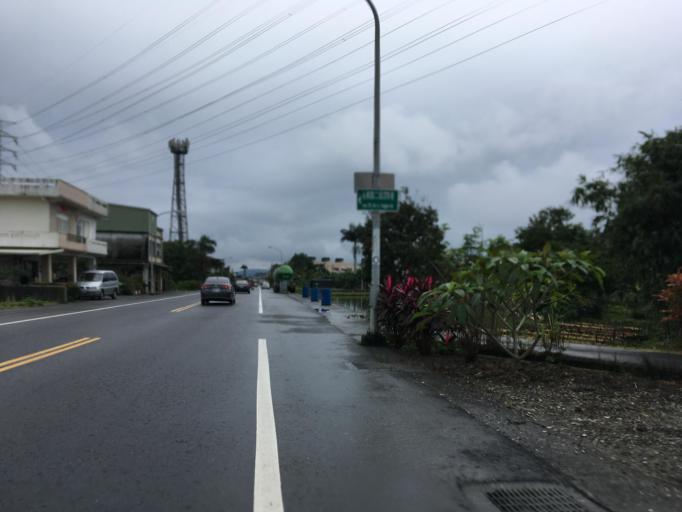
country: TW
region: Taiwan
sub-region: Yilan
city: Yilan
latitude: 24.6595
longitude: 121.7561
